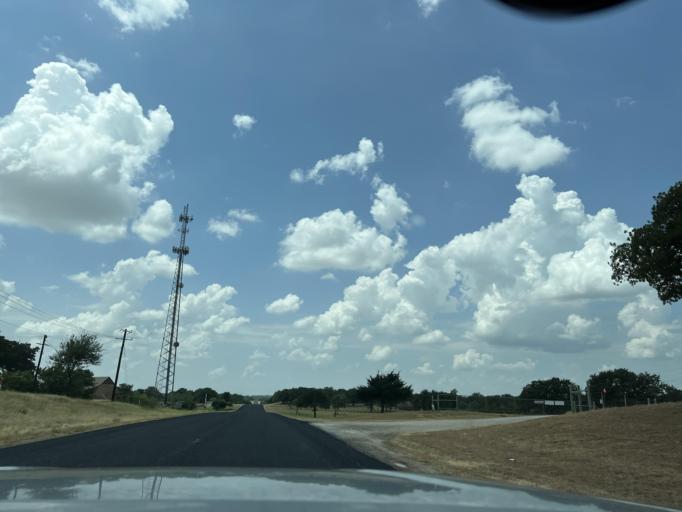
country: US
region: Texas
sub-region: Wise County
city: Boyd
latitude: 33.0660
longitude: -97.6526
